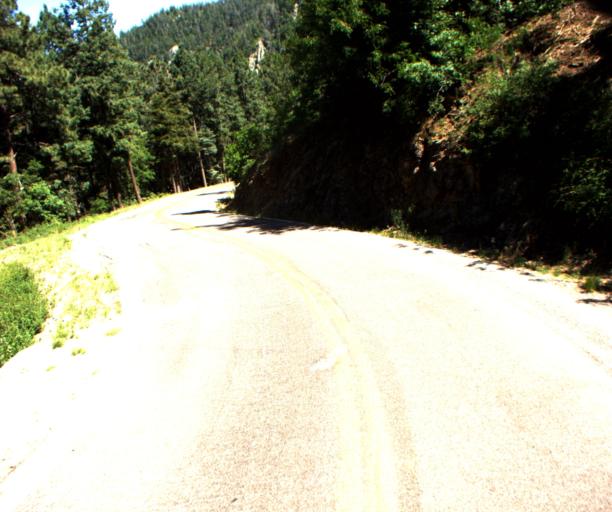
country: US
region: Arizona
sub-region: Graham County
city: Swift Trail Junction
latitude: 32.6288
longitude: -109.8264
